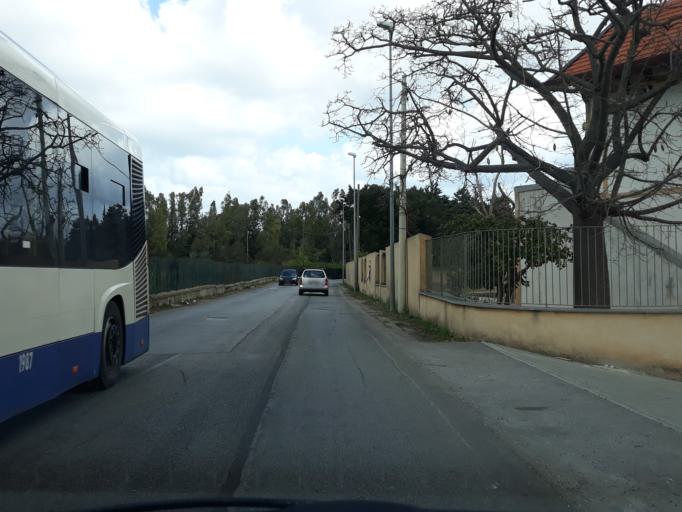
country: IT
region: Sicily
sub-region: Palermo
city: Palermo
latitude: 38.1180
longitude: 13.3044
